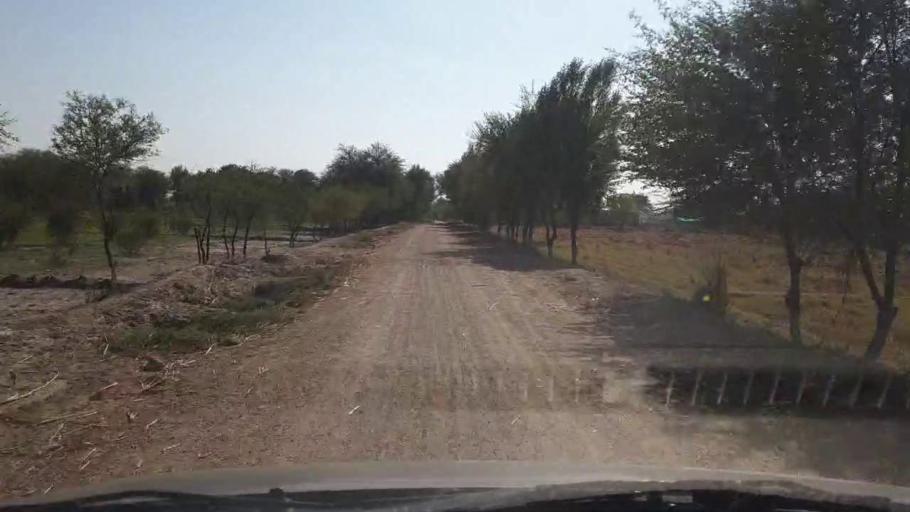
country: PK
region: Sindh
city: Samaro
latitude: 25.1897
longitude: 69.2875
